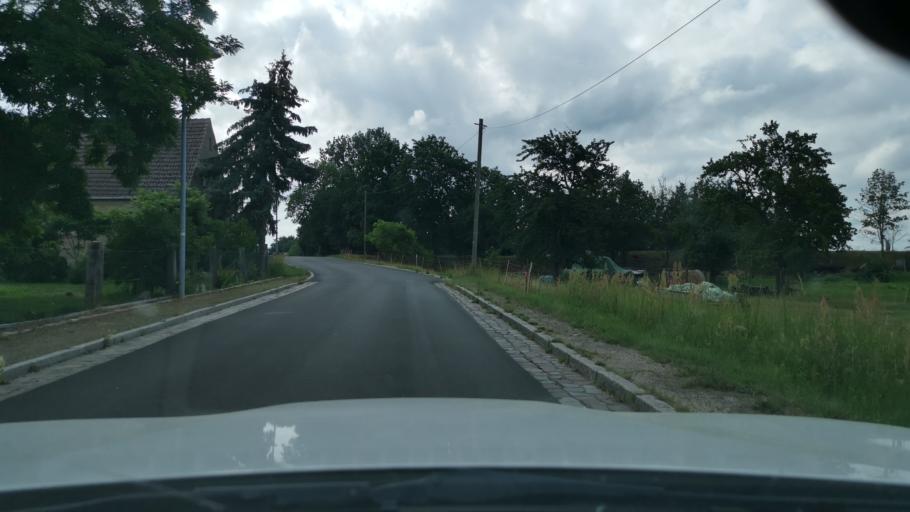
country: DE
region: Saxony
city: Torgau
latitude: 51.6051
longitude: 13.0260
